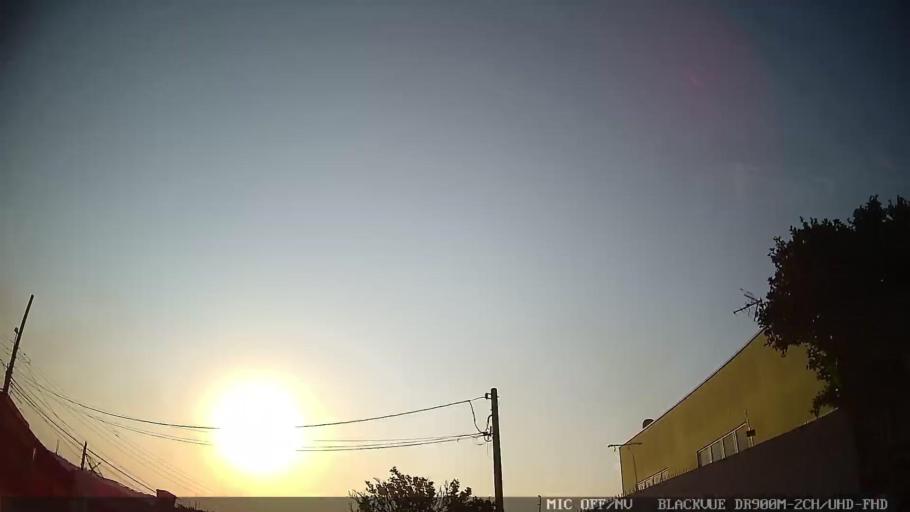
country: BR
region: Sao Paulo
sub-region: Itatiba
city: Itatiba
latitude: -23.0047
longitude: -46.8195
